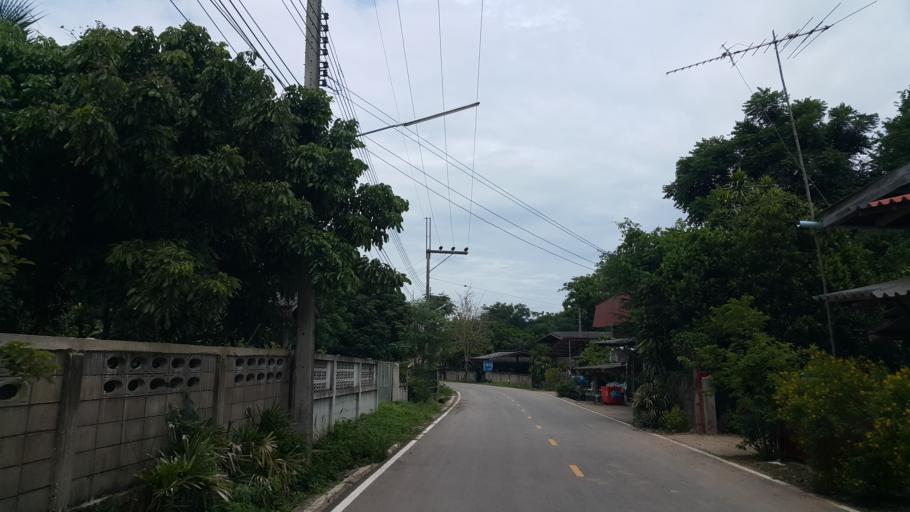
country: TH
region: Lampang
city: Mueang Pan
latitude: 18.7818
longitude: 99.5024
